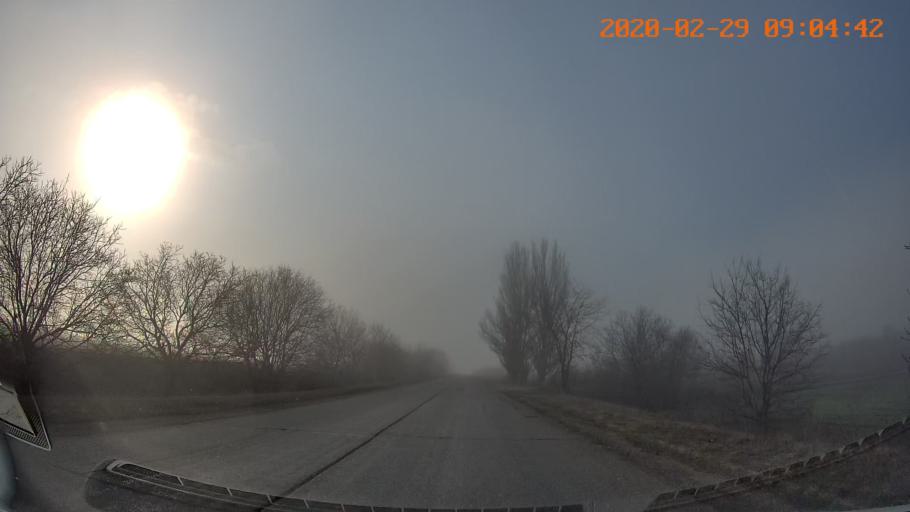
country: MD
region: Telenesti
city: Tiraspolul Nou
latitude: 46.8987
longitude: 29.7372
